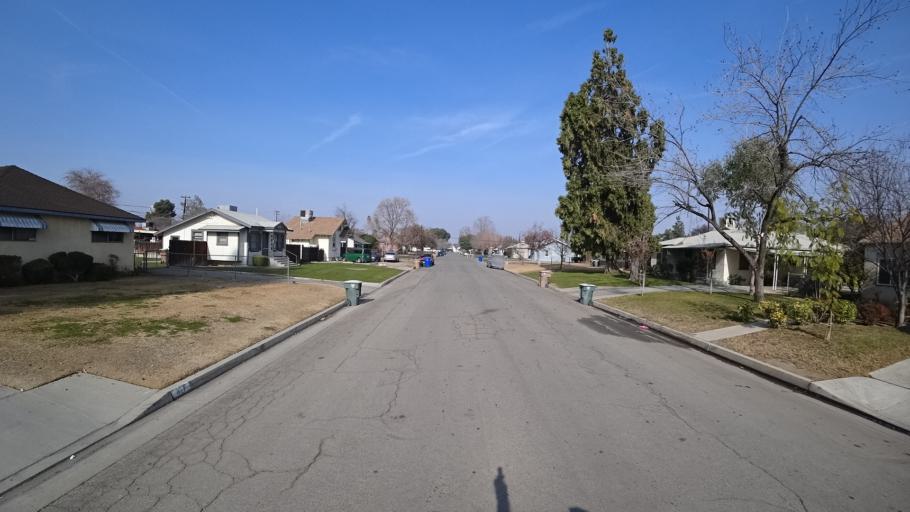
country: US
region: California
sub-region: Kern County
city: Bakersfield
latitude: 35.3624
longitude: -119.0361
